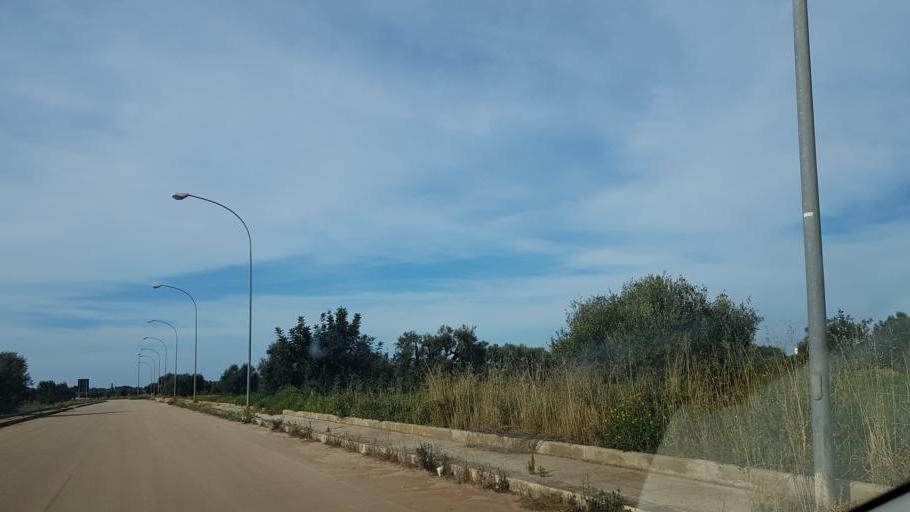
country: IT
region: Apulia
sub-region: Provincia di Brindisi
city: Fasano
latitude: 40.8971
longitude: 17.3574
